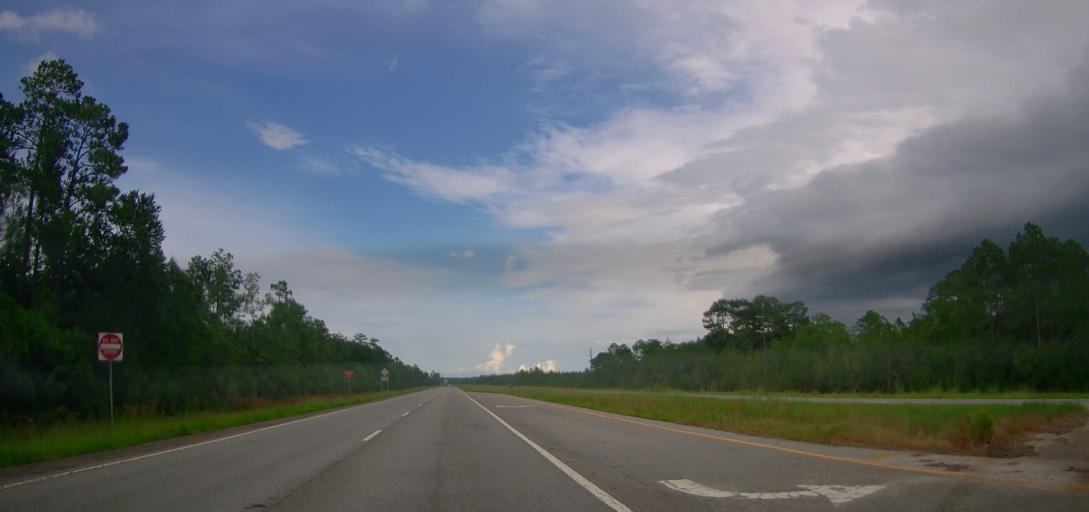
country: US
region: Georgia
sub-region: Pierce County
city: Blackshear
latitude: 31.4413
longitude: -82.0771
